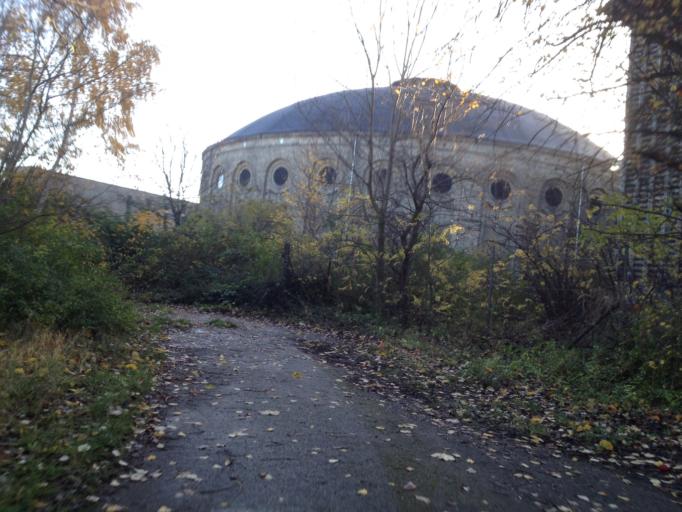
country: DK
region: Capital Region
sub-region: Kobenhavn
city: Copenhagen
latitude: 55.7105
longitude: 12.5809
